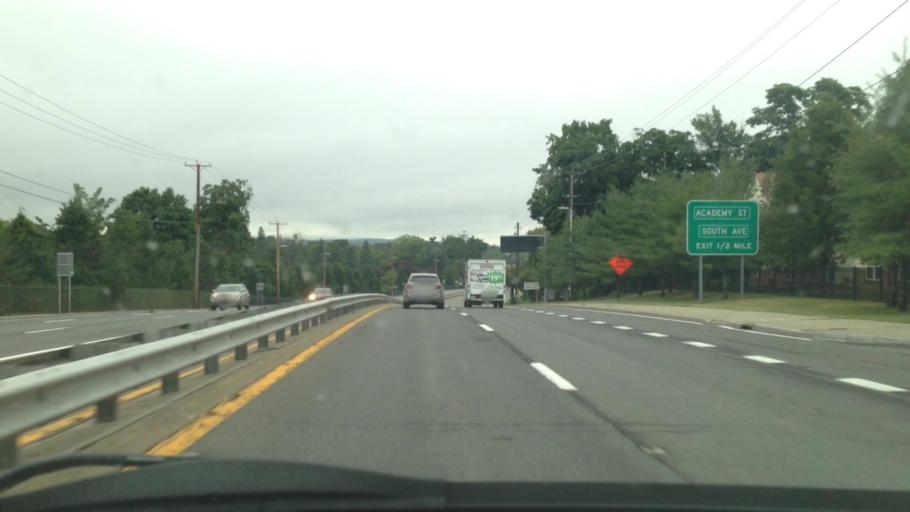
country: US
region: New York
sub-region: Dutchess County
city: Poughkeepsie
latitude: 41.6781
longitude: -73.9288
